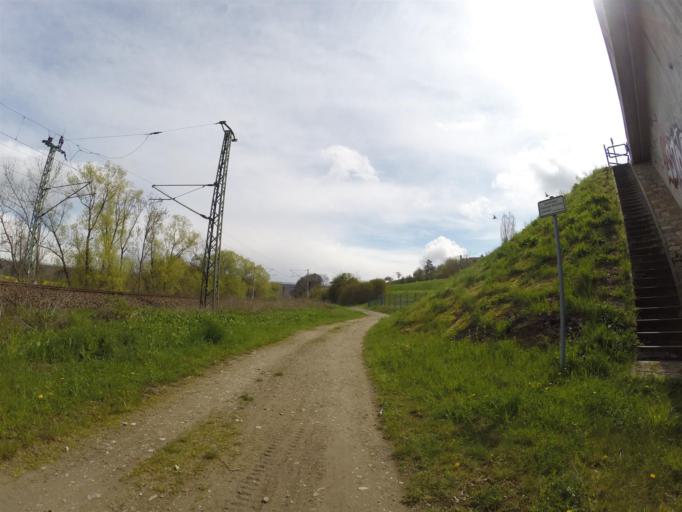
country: DE
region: Thuringia
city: Sulza
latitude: 50.8770
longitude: 11.5942
